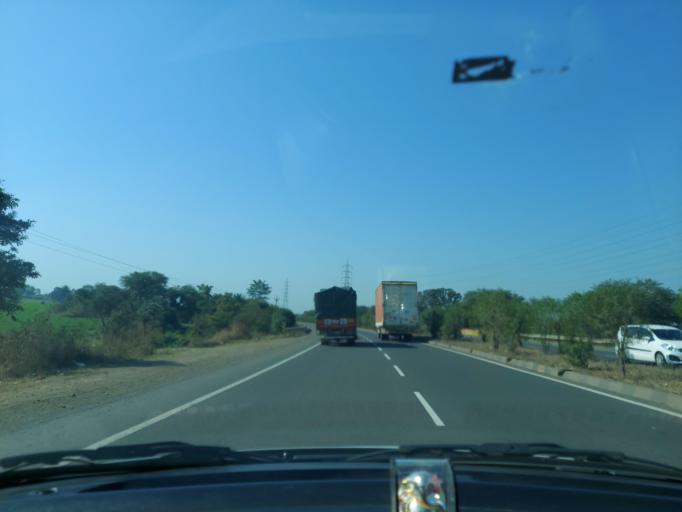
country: IN
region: Madhya Pradesh
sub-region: Indore
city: Pithampur
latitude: 22.5782
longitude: 75.6483
